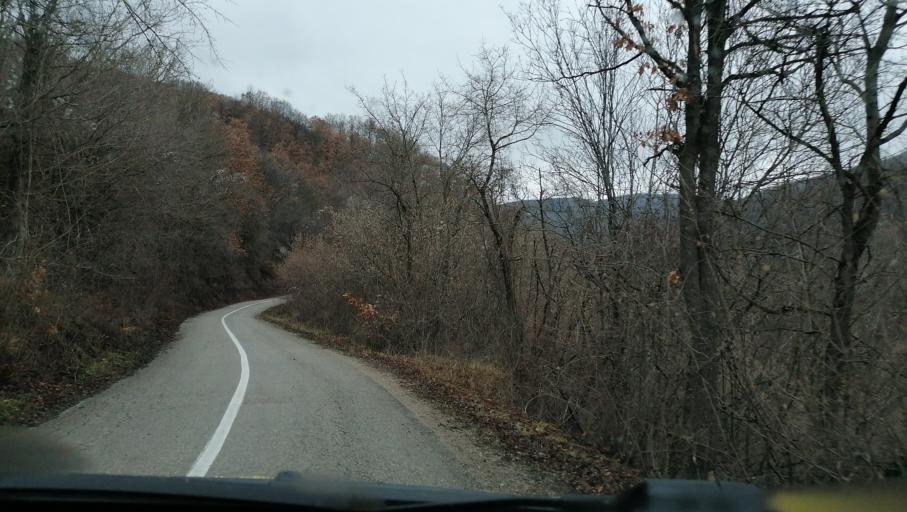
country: RS
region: Central Serbia
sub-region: Pirotski Okrug
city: Dimitrovgrad
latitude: 42.9633
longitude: 22.7826
